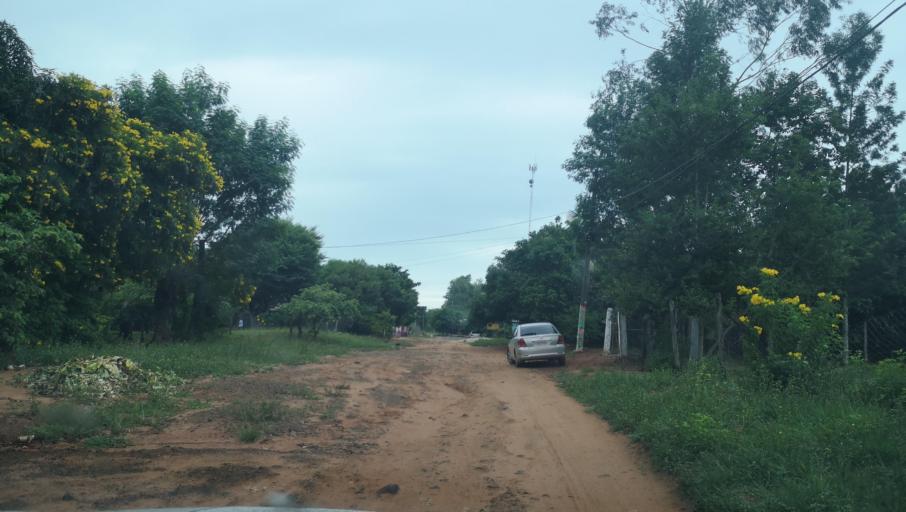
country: PY
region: San Pedro
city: Capiibary
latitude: -24.7260
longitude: -56.0140
